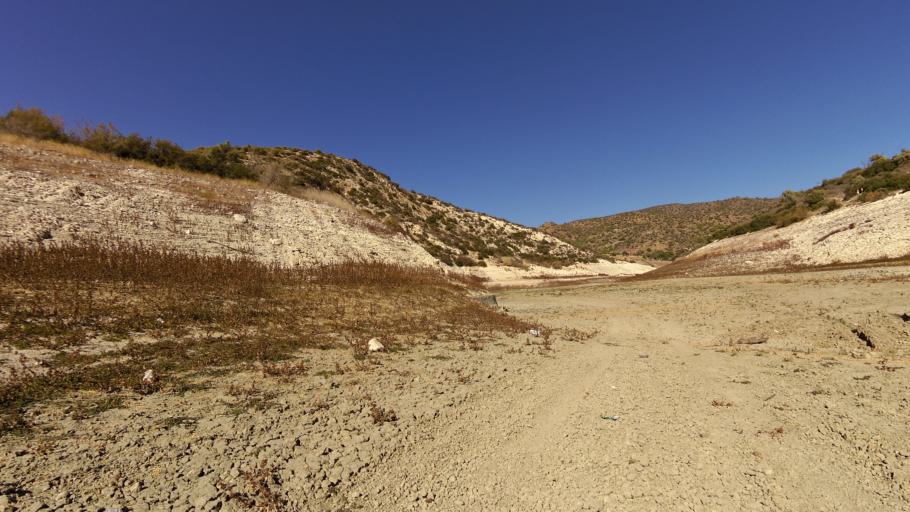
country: CY
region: Limassol
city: Mouttagiaka
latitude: 34.7545
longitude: 33.0912
